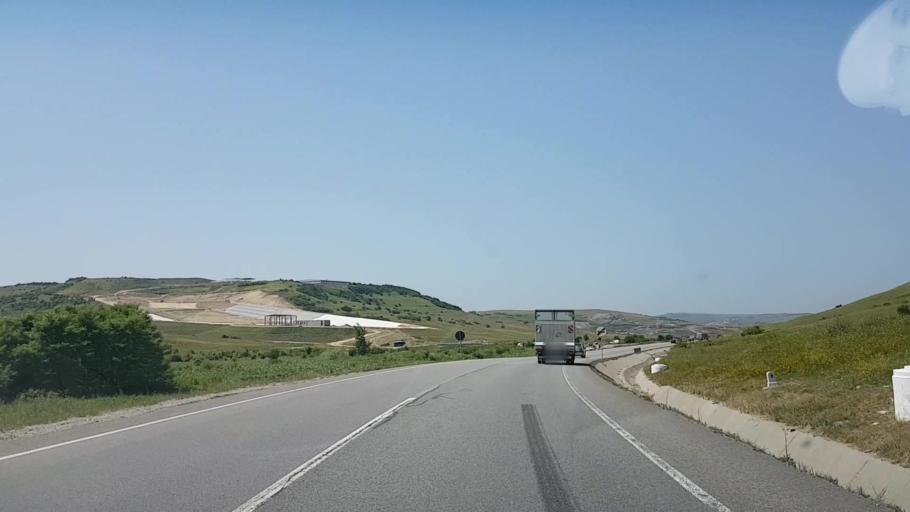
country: RO
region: Cluj
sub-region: Comuna Apahida
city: Dezmir
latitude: 46.7475
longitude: 23.7088
